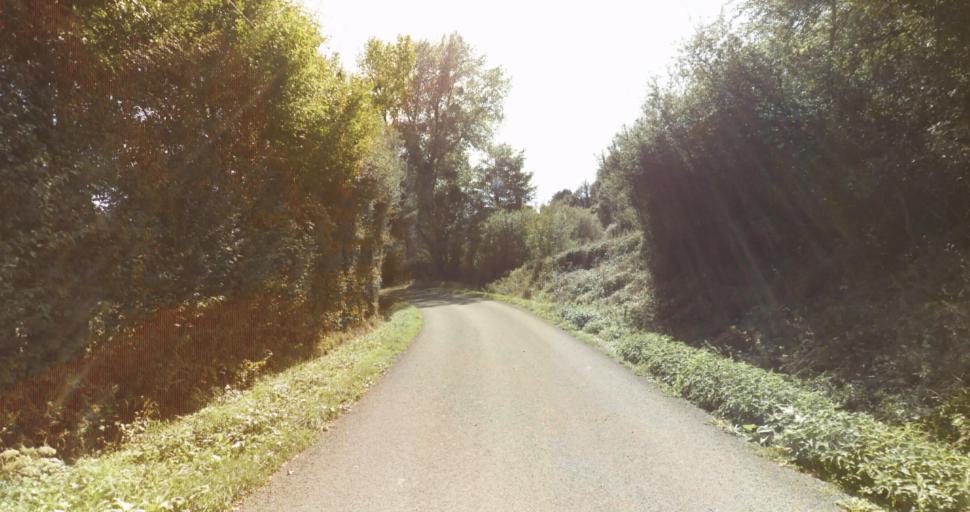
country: FR
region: Lower Normandy
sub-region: Departement de l'Orne
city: Gace
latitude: 48.7325
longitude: 0.2366
